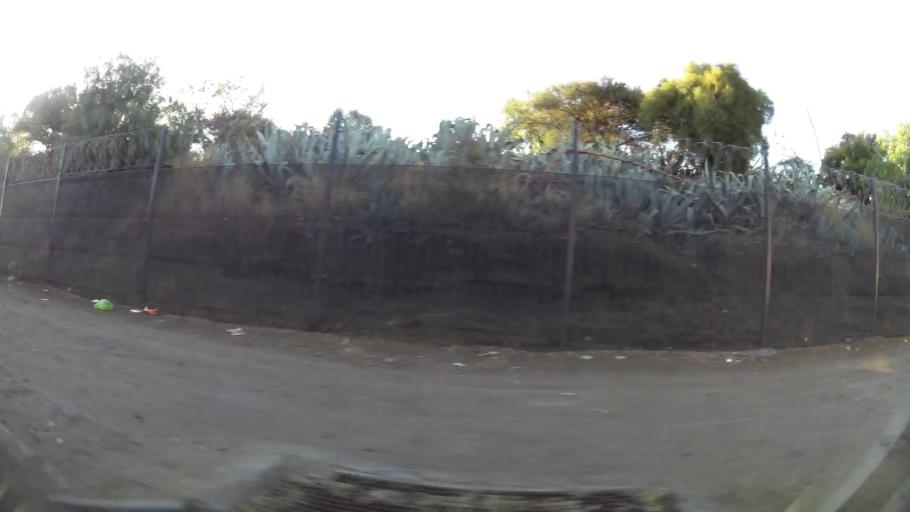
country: ZA
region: Northern Cape
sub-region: Frances Baard District Municipality
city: Kimberley
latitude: -28.7422
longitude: 24.7561
